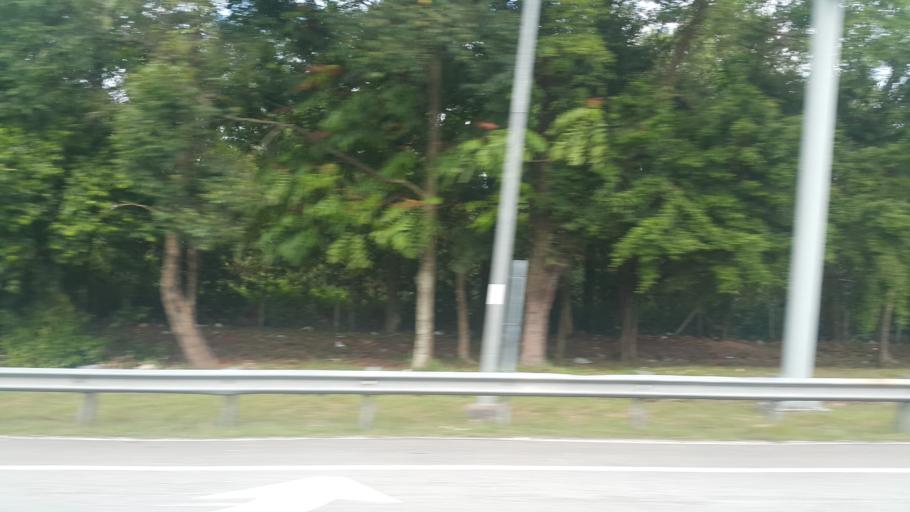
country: MY
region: Johor
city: Skudai
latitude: 1.4480
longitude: 103.6154
